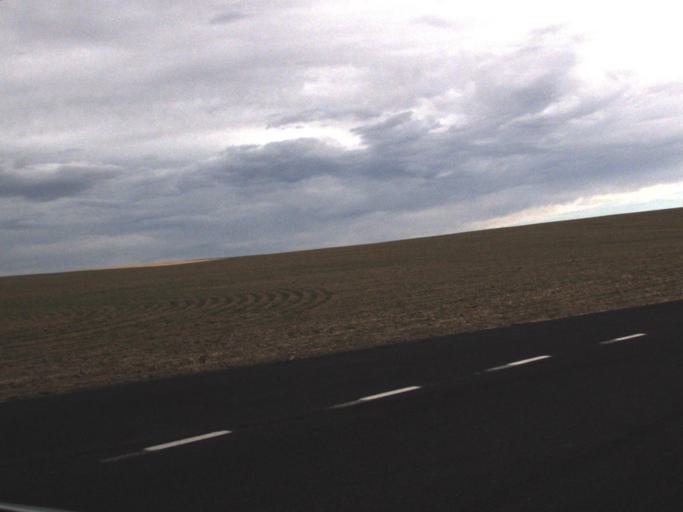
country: US
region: Washington
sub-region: Okanogan County
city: Coulee Dam
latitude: 47.6121
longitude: -118.7845
